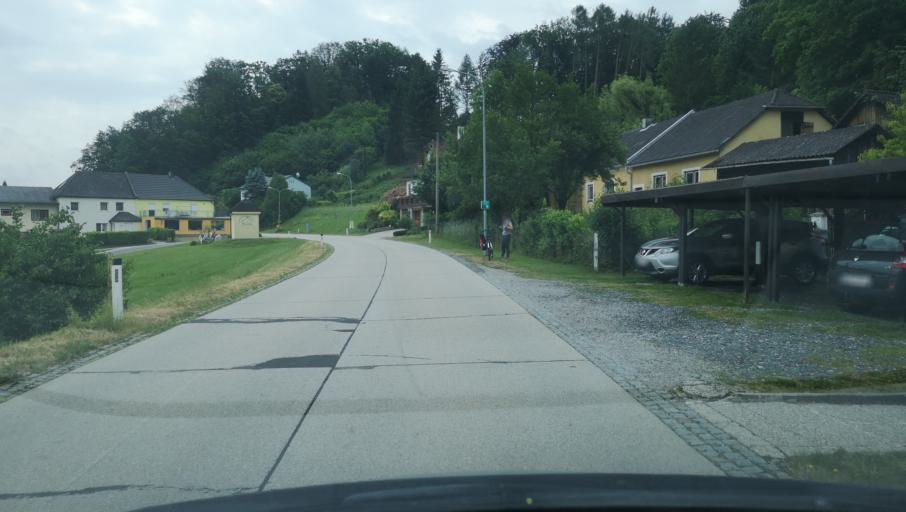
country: AT
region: Lower Austria
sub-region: Politischer Bezirk Melk
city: Ybbs an der Donau
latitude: 48.1907
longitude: 15.0607
